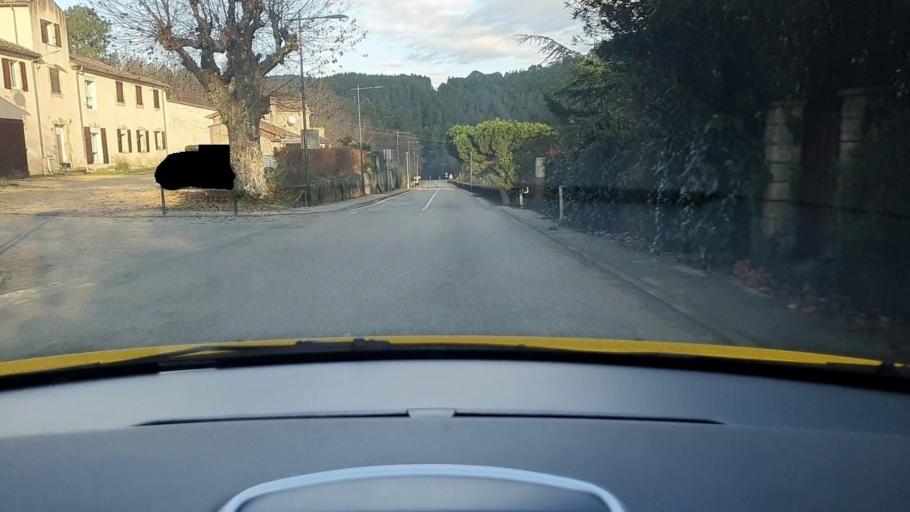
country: FR
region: Languedoc-Roussillon
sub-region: Departement du Gard
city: Les Salles-du-Gardon
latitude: 44.2477
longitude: 4.0490
